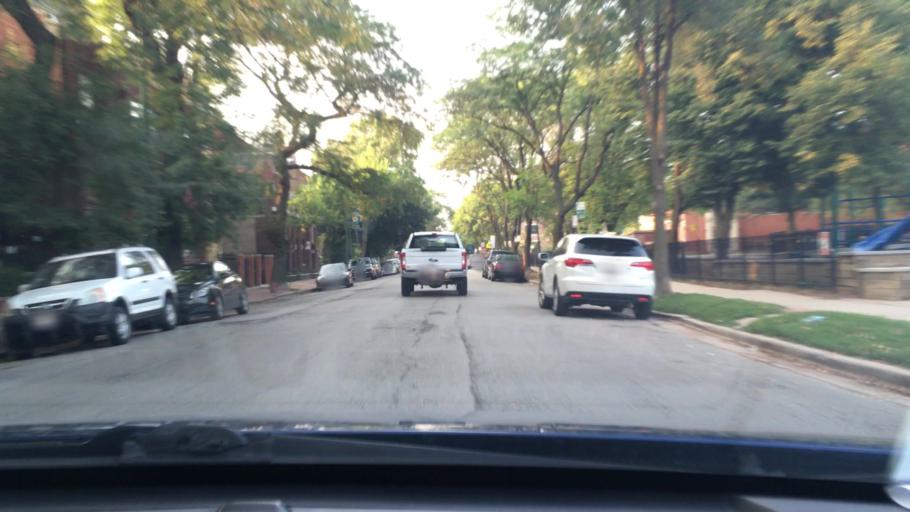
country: US
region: Illinois
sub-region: Cook County
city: Chicago
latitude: 41.9222
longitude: -87.6583
